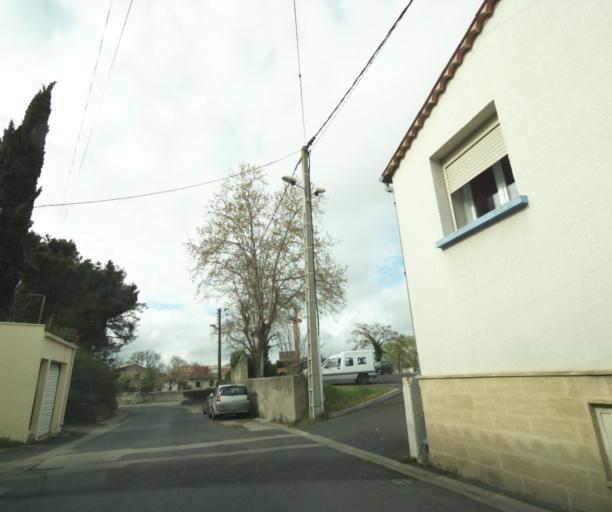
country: FR
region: Languedoc-Roussillon
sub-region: Departement de l'Herault
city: Fabregues
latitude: 43.5504
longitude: 3.7809
